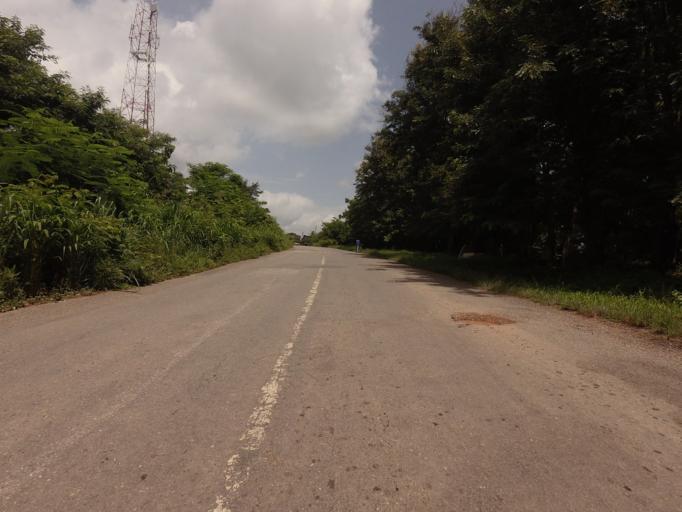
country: GH
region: Volta
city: Ho
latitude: 6.7168
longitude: 0.3385
